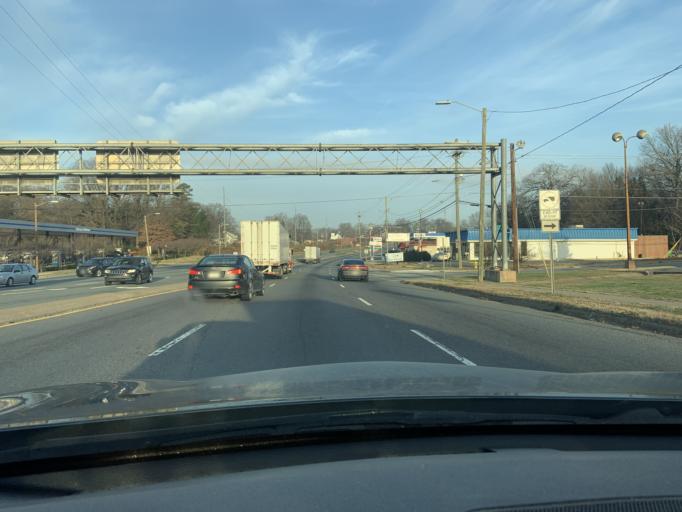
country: US
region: North Carolina
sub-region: Mecklenburg County
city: Charlotte
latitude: 35.2629
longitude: -80.8793
